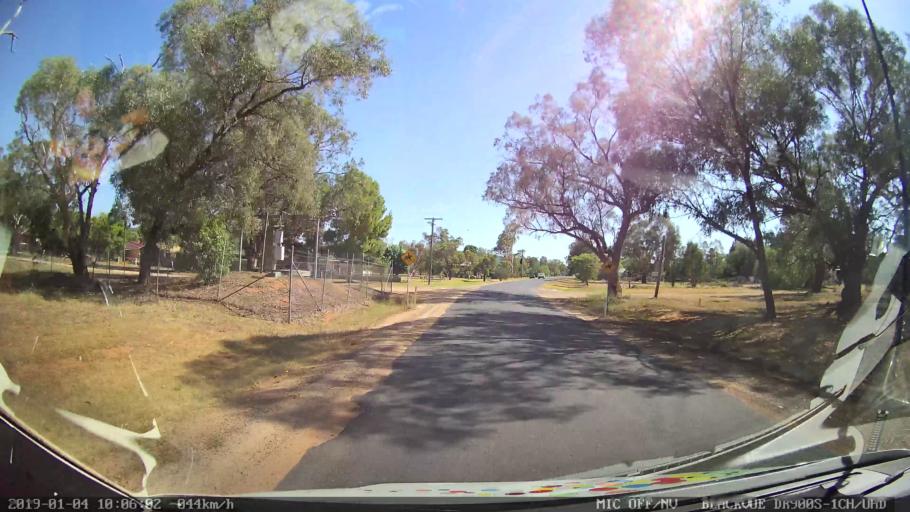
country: AU
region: New South Wales
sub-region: Cabonne
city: Canowindra
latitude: -33.4360
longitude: 148.3671
